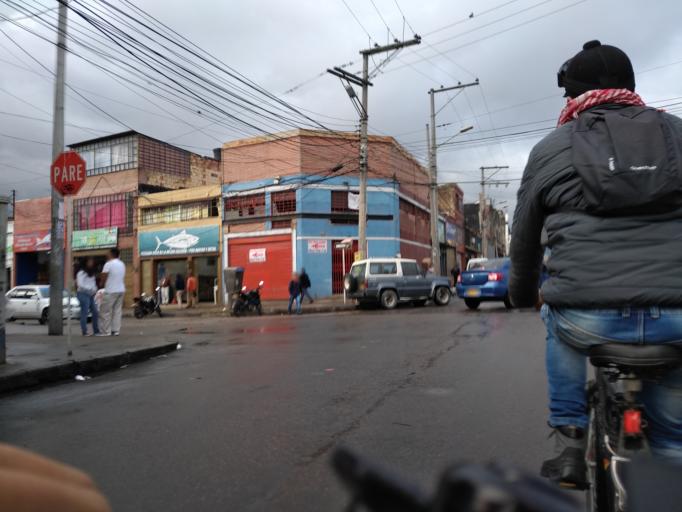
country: CO
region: Bogota D.C.
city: Bogota
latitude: 4.6028
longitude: -74.0846
